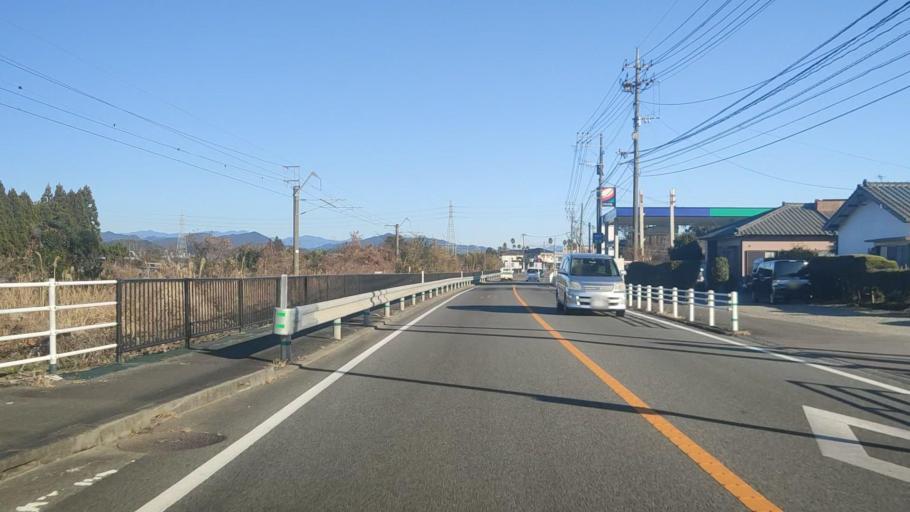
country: JP
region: Miyazaki
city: Nobeoka
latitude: 32.3884
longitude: 131.6275
